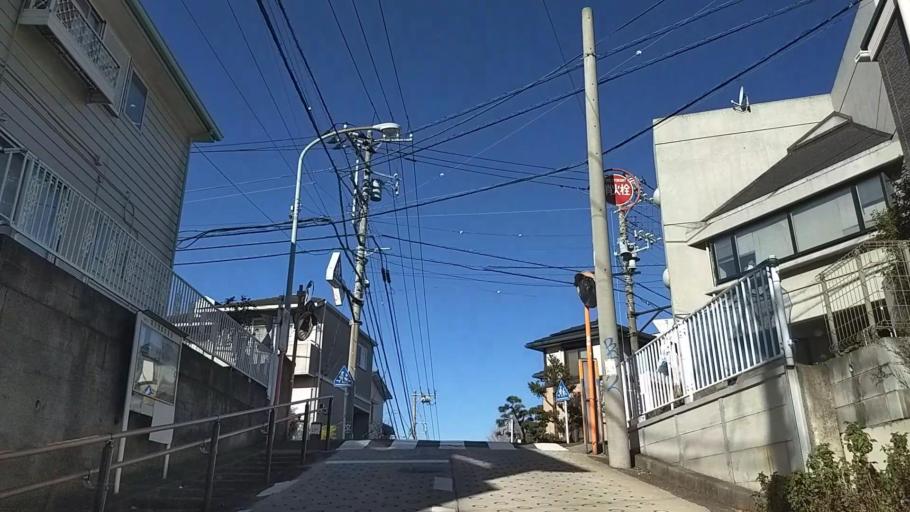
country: JP
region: Kanagawa
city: Yokohama
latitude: 35.4483
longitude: 139.6201
